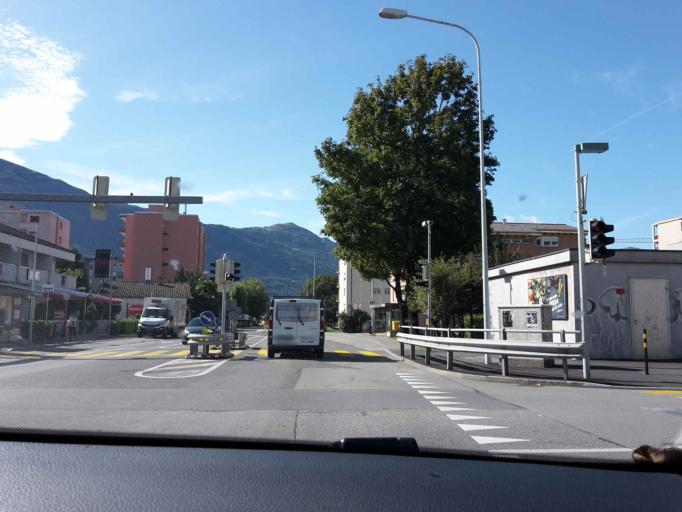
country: CH
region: Ticino
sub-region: Bellinzona District
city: Bellinzona
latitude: 46.1874
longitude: 9.0147
